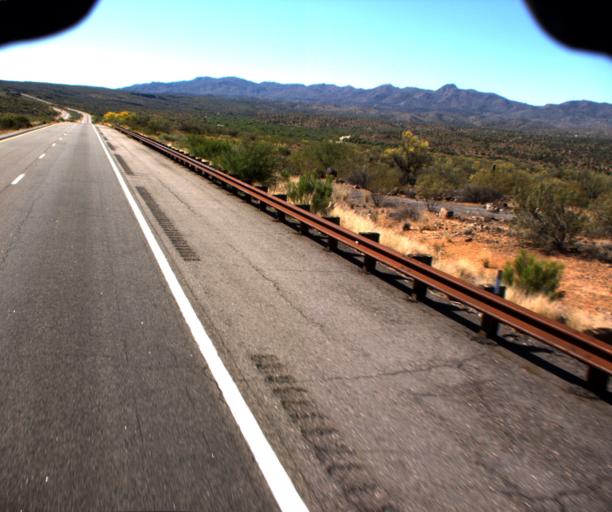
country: US
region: Arizona
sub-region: Yavapai County
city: Bagdad
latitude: 34.5182
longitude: -113.4216
